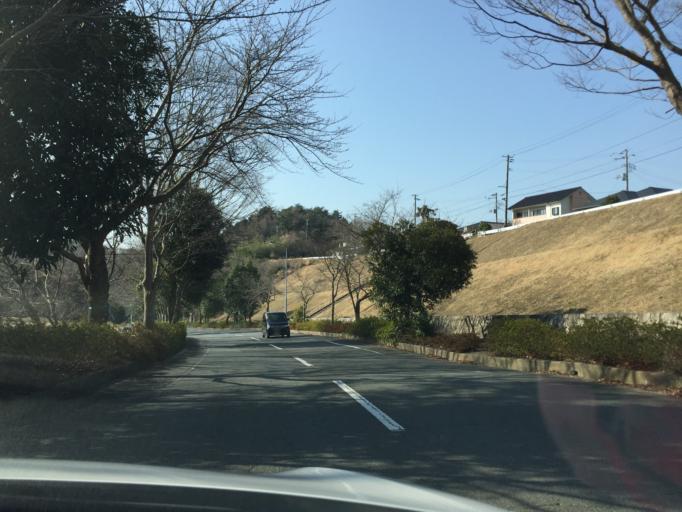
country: JP
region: Fukushima
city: Iwaki
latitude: 36.9635
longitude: 140.9332
